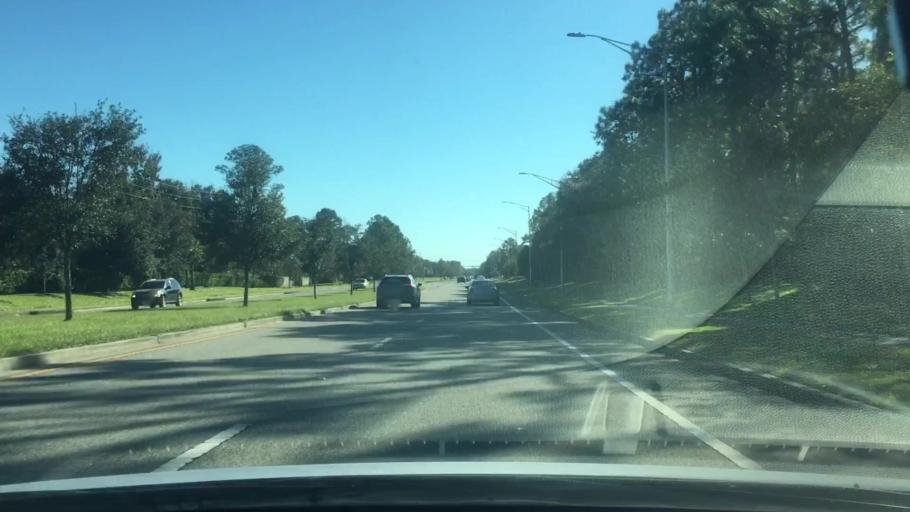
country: US
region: Florida
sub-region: Duval County
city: Neptune Beach
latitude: 30.3050
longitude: -81.4593
